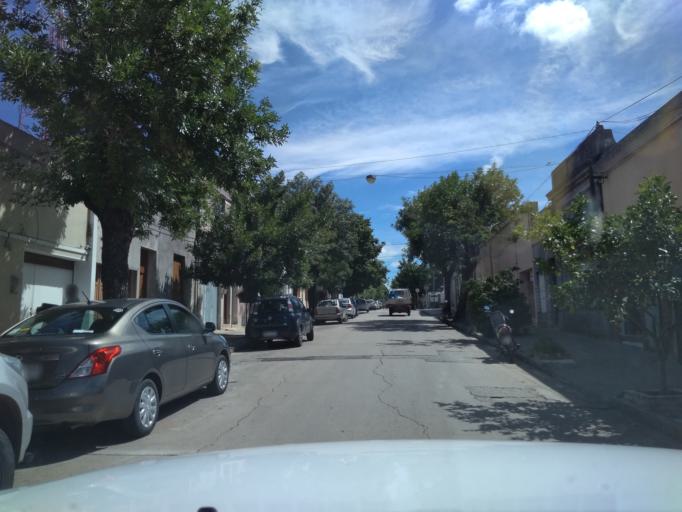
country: UY
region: Florida
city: Florida
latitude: -34.0979
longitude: -56.2136
